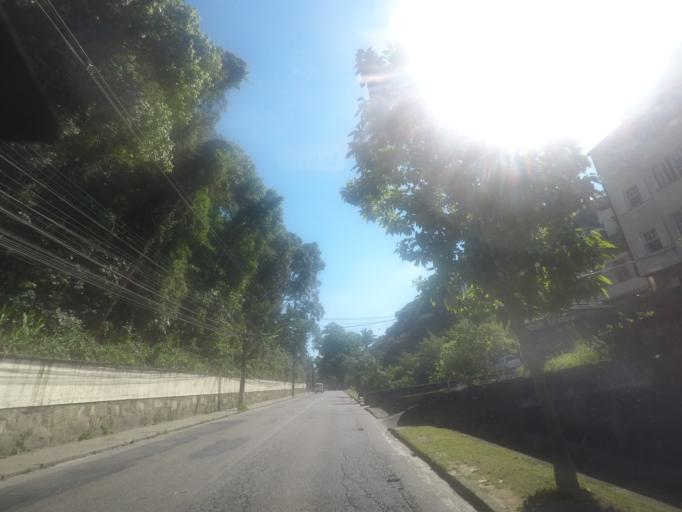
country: BR
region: Rio de Janeiro
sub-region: Petropolis
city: Petropolis
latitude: -22.5172
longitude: -43.1854
